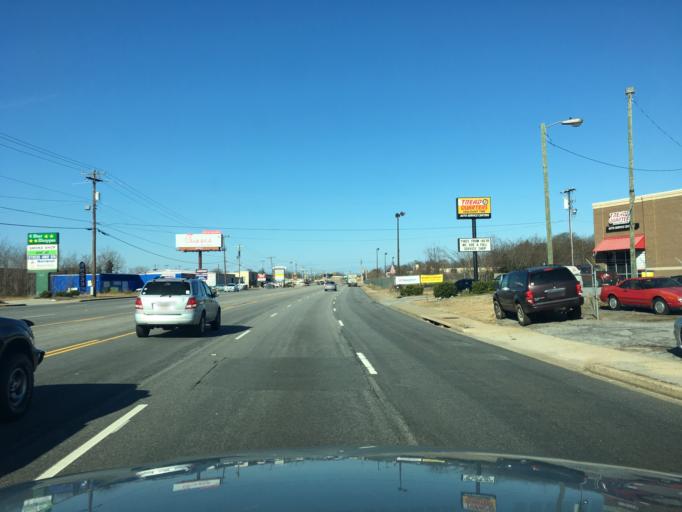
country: US
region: South Carolina
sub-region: Greenville County
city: Sans Souci
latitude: 34.8876
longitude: -82.3963
